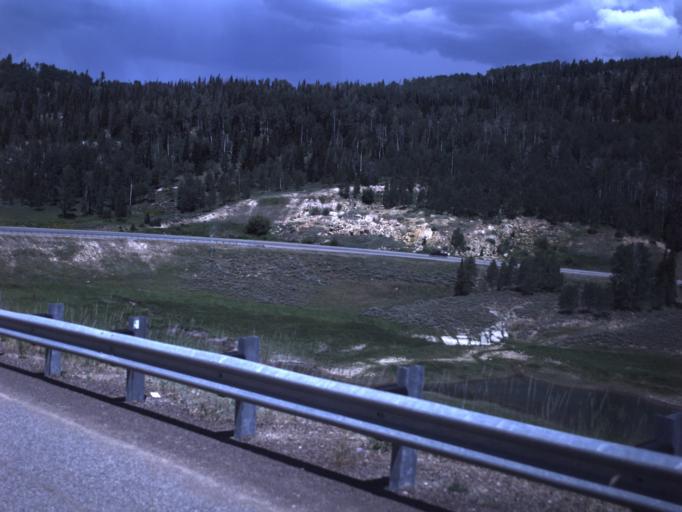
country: US
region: Utah
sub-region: Sanpete County
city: Fairview
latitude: 39.5848
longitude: -111.2419
